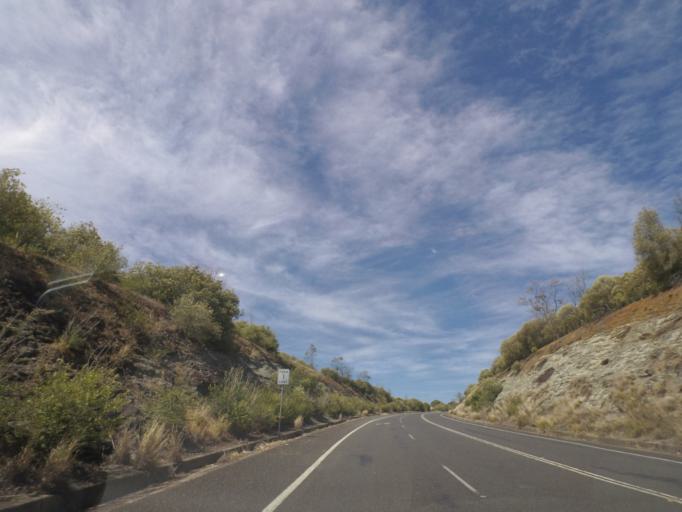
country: AU
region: New South Wales
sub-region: Wollondilly
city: Douglas Park
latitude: -34.1502
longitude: 150.6706
